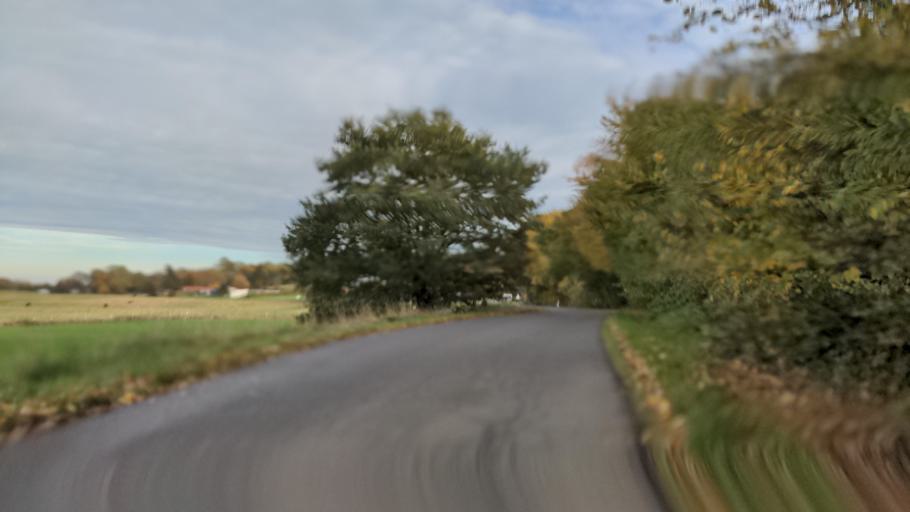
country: DE
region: Schleswig-Holstein
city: Malente
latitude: 54.1123
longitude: 10.5381
